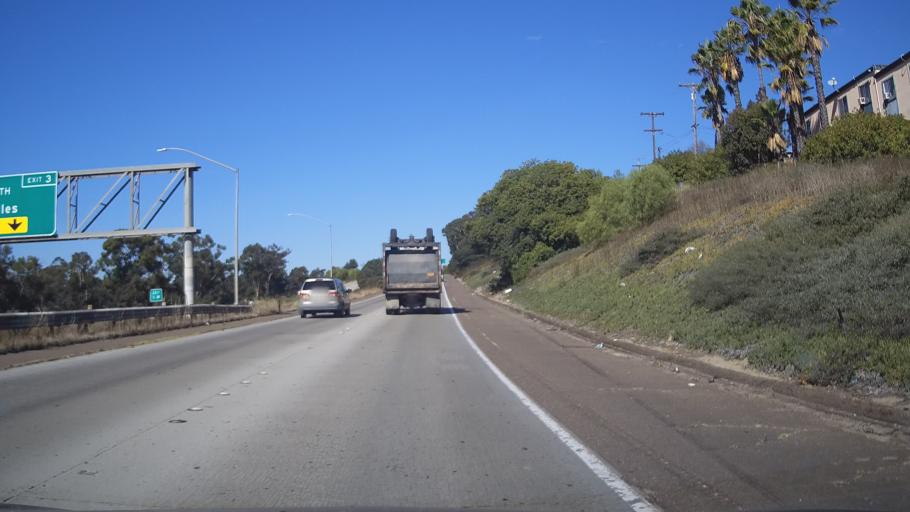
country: US
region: California
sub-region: San Diego County
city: San Diego
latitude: 32.7339
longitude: -117.1115
